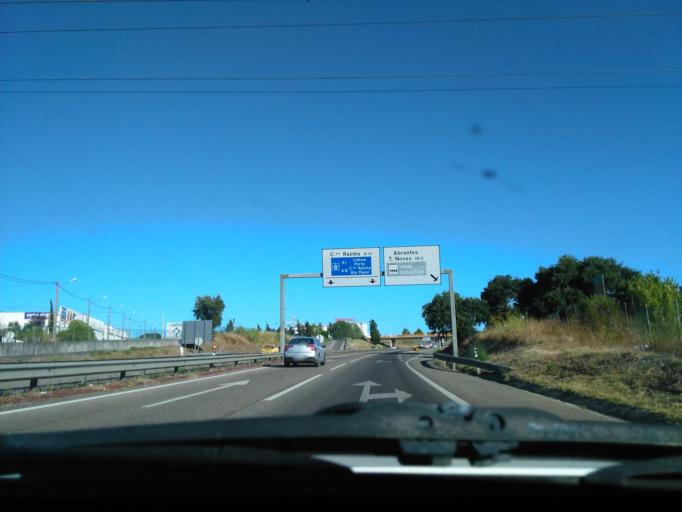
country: PT
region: Santarem
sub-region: Santarem
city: Santarem
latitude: 39.2576
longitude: -8.7019
